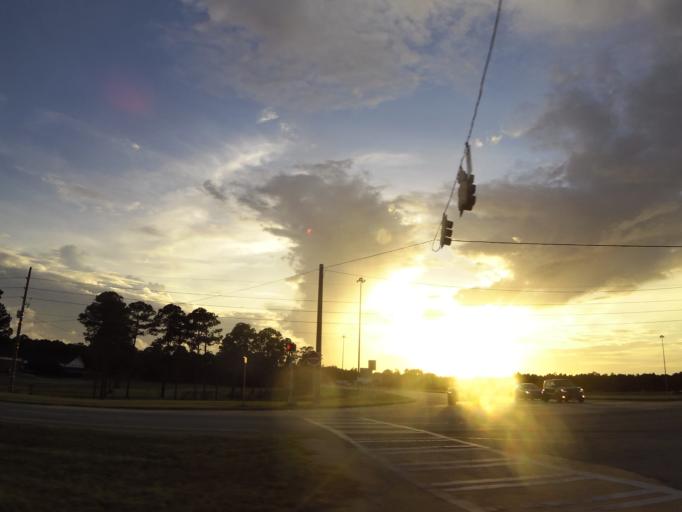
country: US
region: Georgia
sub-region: Glynn County
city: Dock Junction
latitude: 31.2396
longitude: -81.5021
